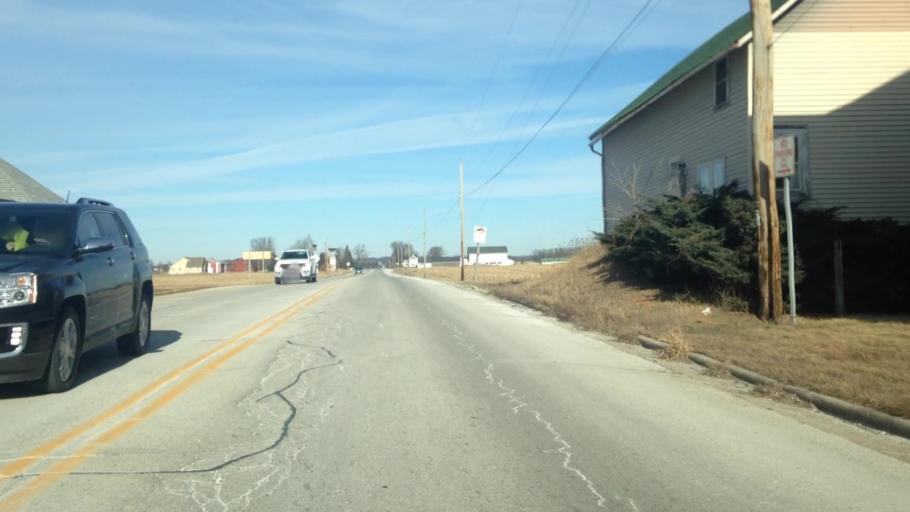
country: US
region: Wisconsin
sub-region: Washington County
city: Richfield
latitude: 43.2660
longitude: -88.2615
